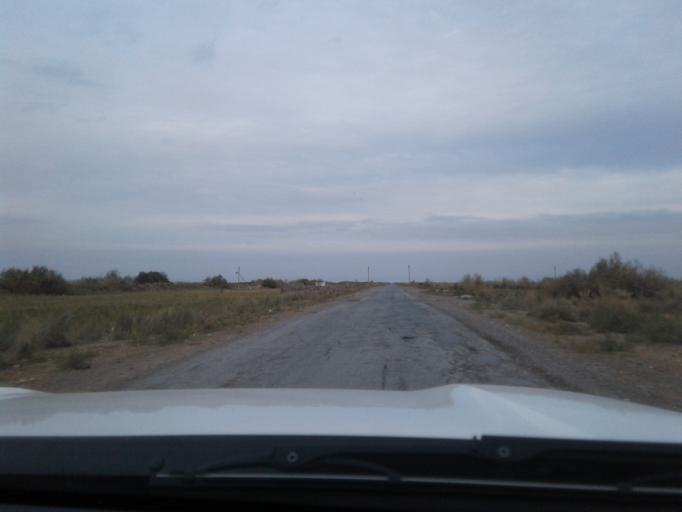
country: TM
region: Mary
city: Mary
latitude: 38.0162
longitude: 61.8576
